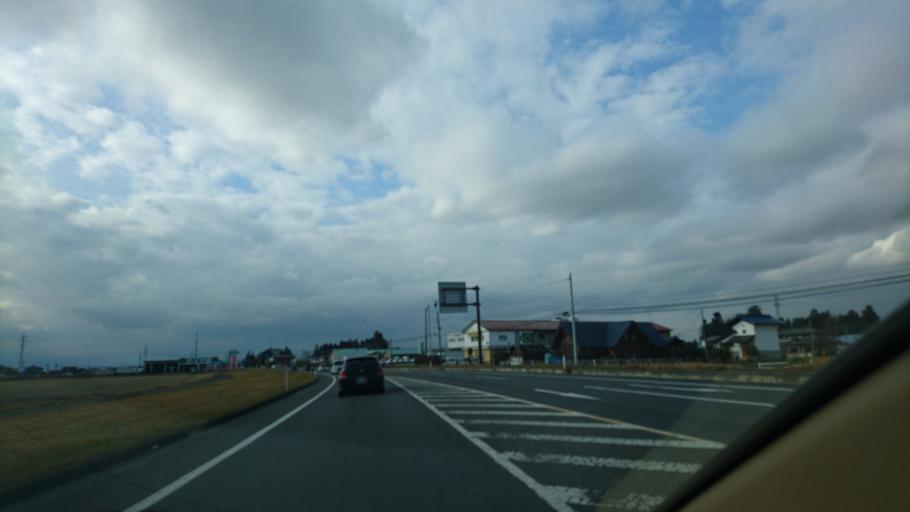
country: JP
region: Miyagi
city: Kogota
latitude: 38.5595
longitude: 141.0338
